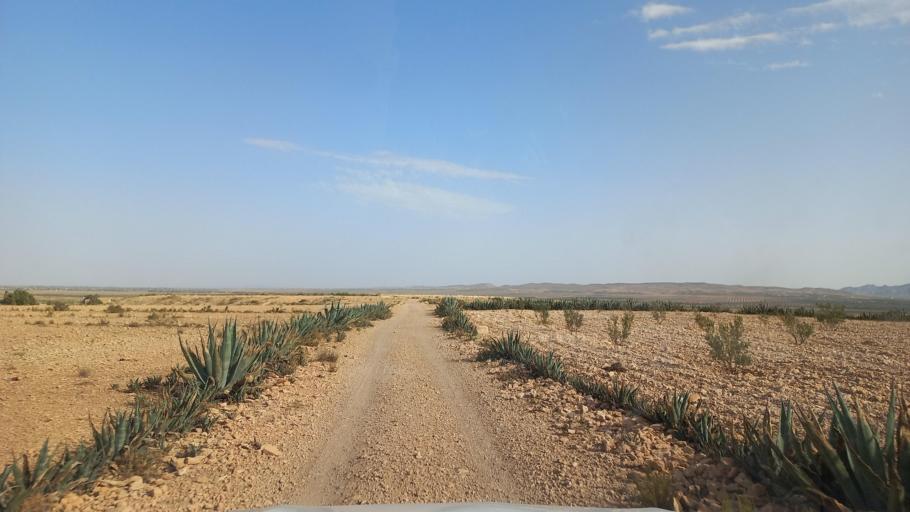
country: TN
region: Al Qasrayn
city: Kasserine
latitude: 35.2596
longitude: 8.9289
